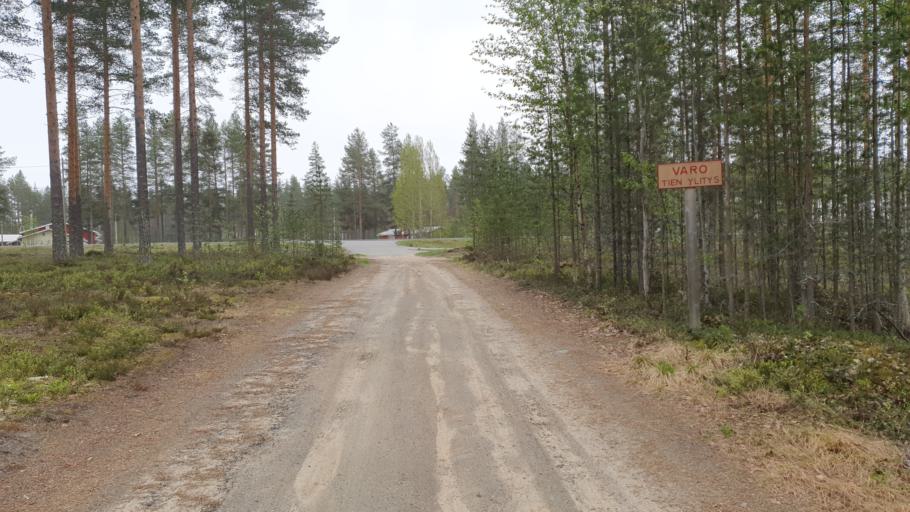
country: FI
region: Kainuu
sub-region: Kehys-Kainuu
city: Kuhmo
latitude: 64.0961
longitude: 29.4659
